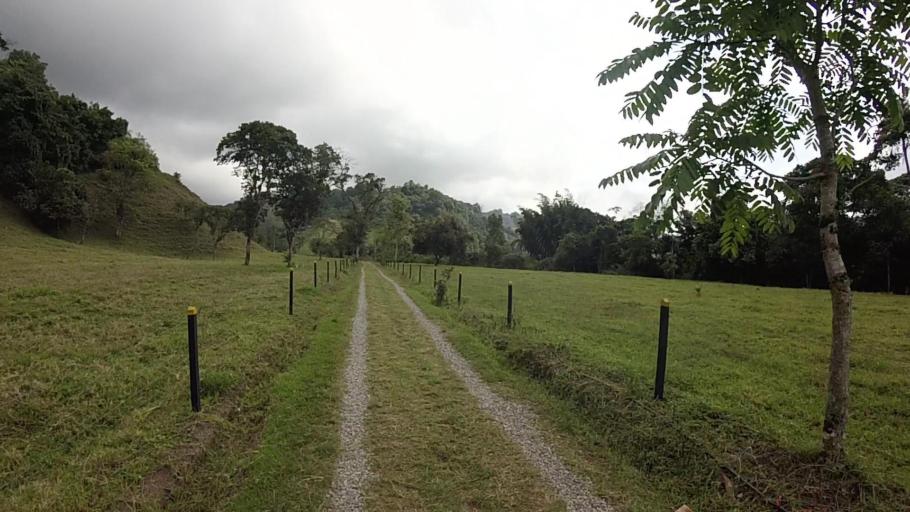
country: CO
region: Quindio
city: Salento
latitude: 4.6477
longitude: -75.5799
